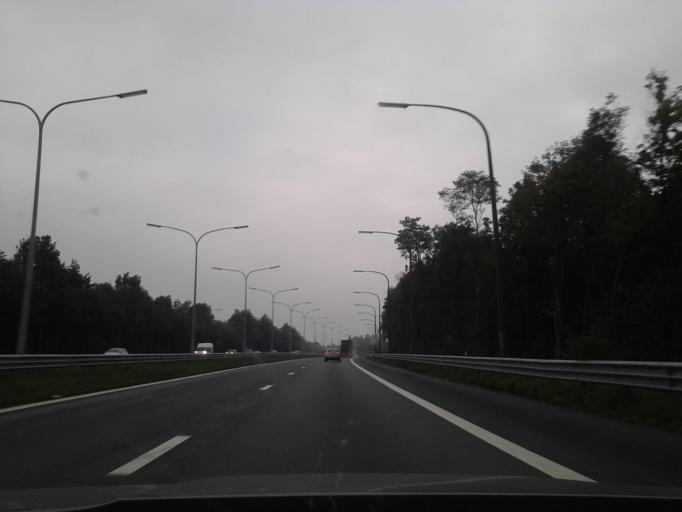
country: BE
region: Wallonia
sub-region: Province du Brabant Wallon
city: Nivelles
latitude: 50.5750
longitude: 4.3042
